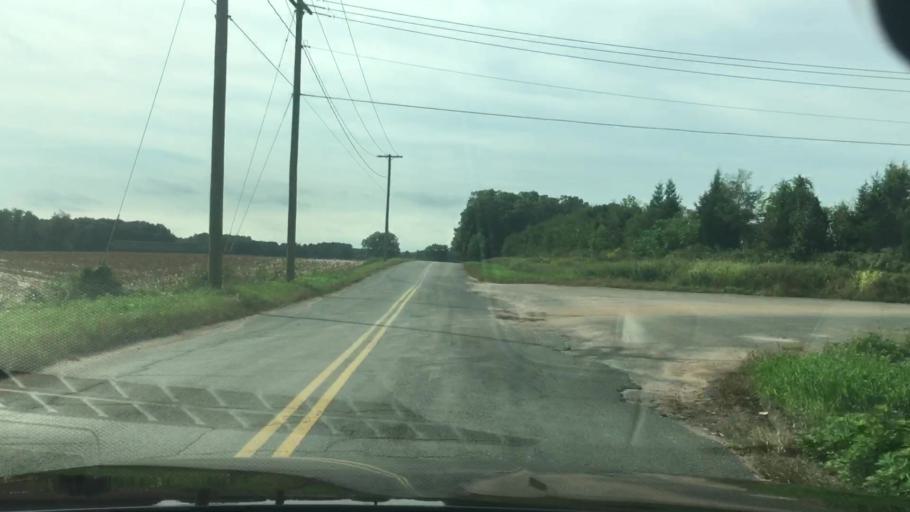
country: US
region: Connecticut
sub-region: Hartford County
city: Broad Brook
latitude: 41.8816
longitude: -72.5446
